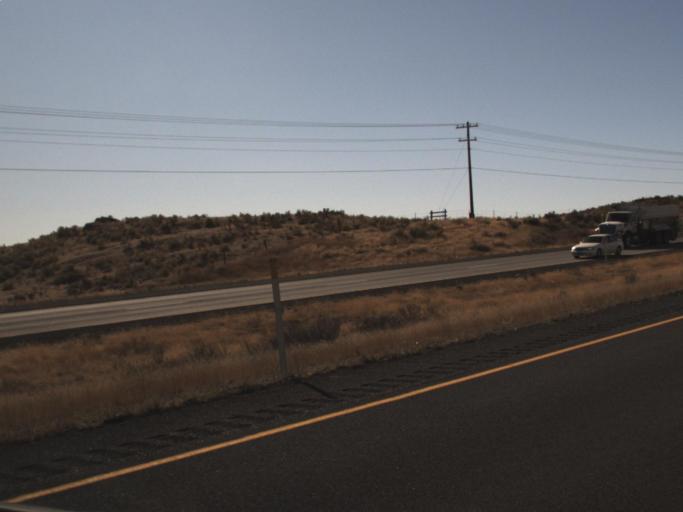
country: US
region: Washington
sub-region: Franklin County
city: Pasco
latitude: 46.4270
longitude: -119.0270
